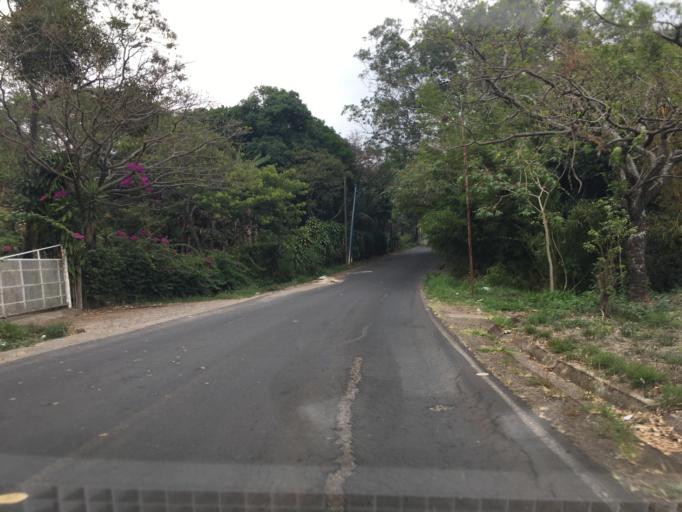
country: GT
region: Guatemala
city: Fraijanes
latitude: 14.3977
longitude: -90.4808
